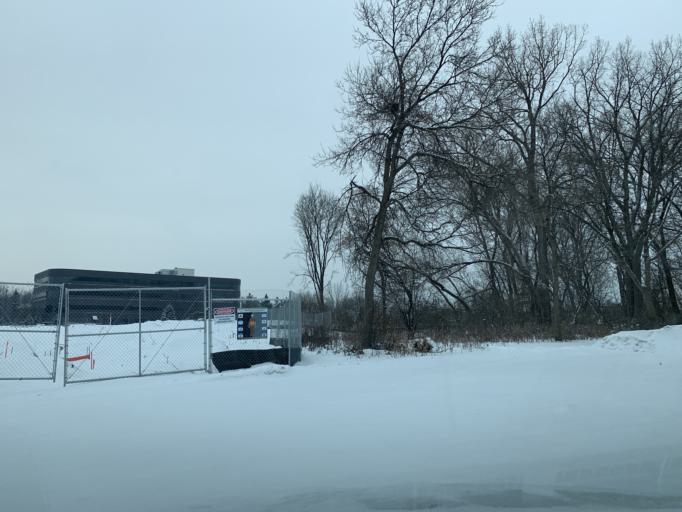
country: US
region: Minnesota
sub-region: Hennepin County
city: Saint Louis Park
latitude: 44.9451
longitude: -93.3379
